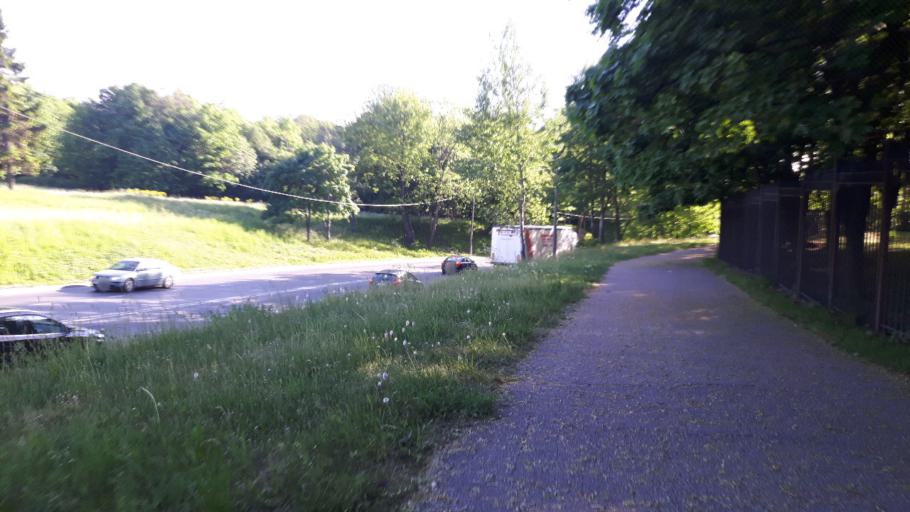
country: EE
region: Harju
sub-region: Tallinna linn
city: Tallinn
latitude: 59.4433
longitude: 24.8110
